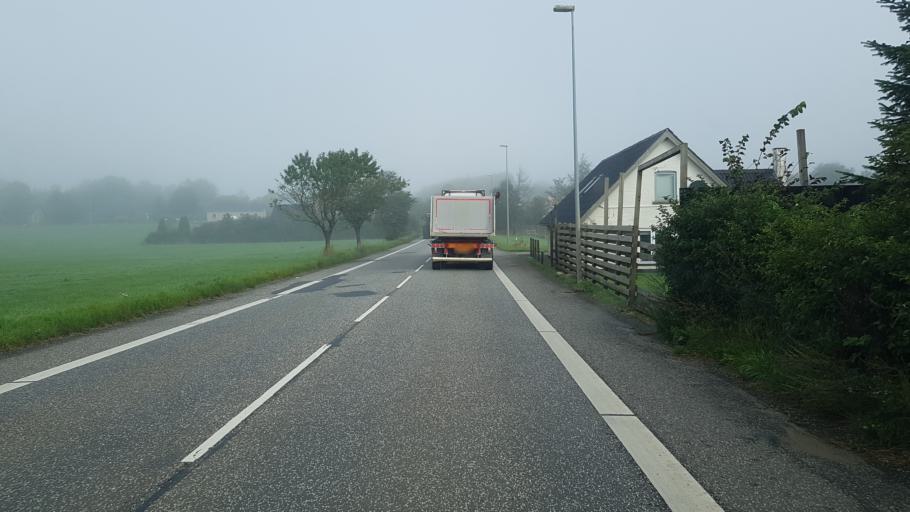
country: DK
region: Central Jutland
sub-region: Viborg Kommune
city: Karup
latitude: 56.3215
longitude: 9.2671
